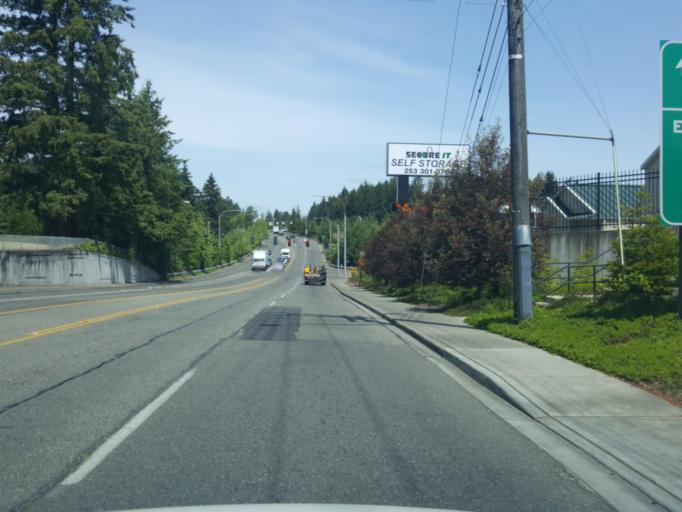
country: US
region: Washington
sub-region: Pierce County
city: Fircrest
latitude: 47.2394
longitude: -122.5049
